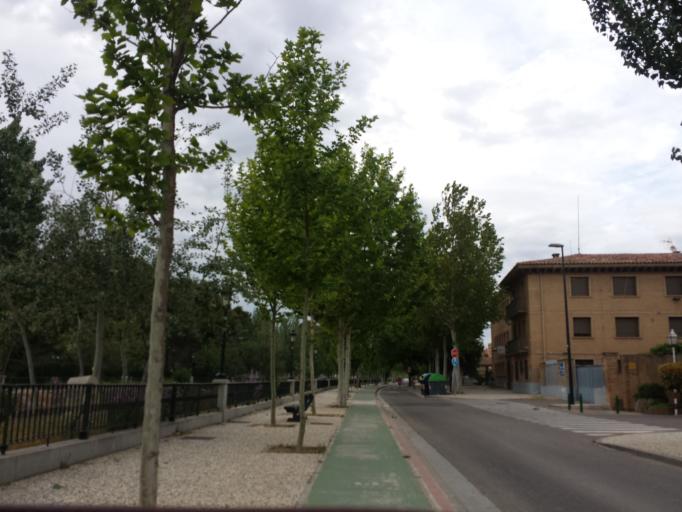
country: ES
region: Aragon
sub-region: Provincia de Zaragoza
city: Delicias
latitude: 41.6245
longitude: -0.9065
